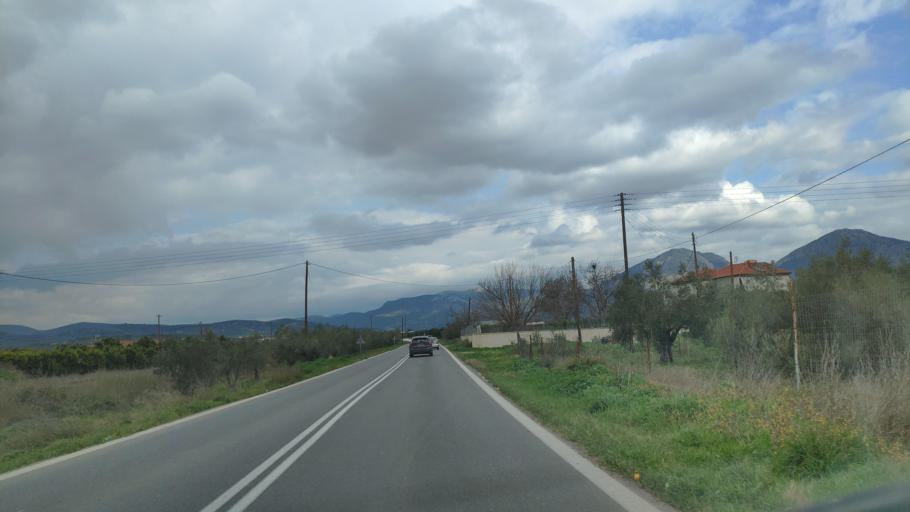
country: GR
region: Peloponnese
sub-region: Nomos Argolidos
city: Koutsopodi
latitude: 37.6928
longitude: 22.7207
